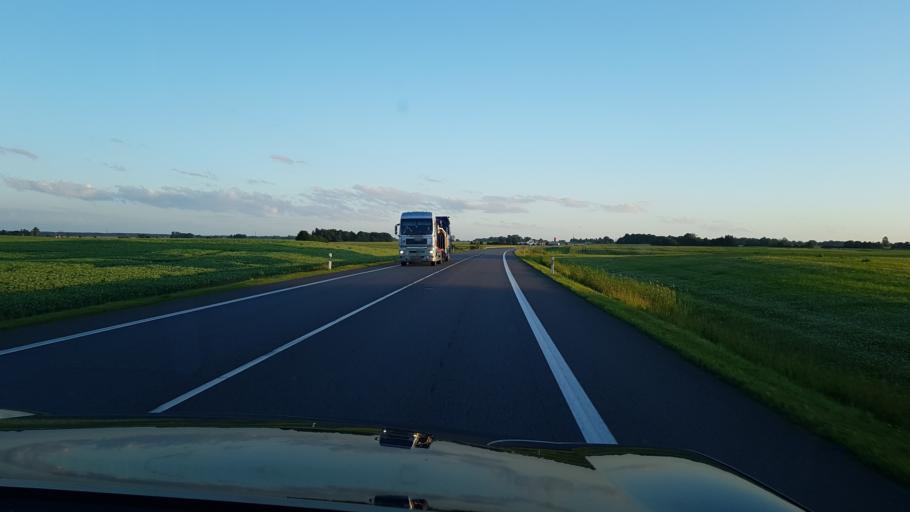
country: LT
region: Kauno apskritis
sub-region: Kauno rajonas
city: Mastaiciai
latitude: 54.7456
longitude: 23.7219
